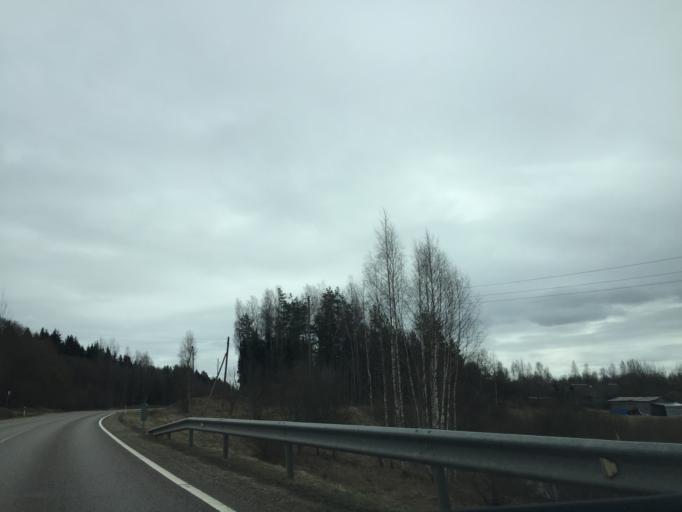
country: LV
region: Kraslavas Rajons
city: Kraslava
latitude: 55.9097
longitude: 27.0918
